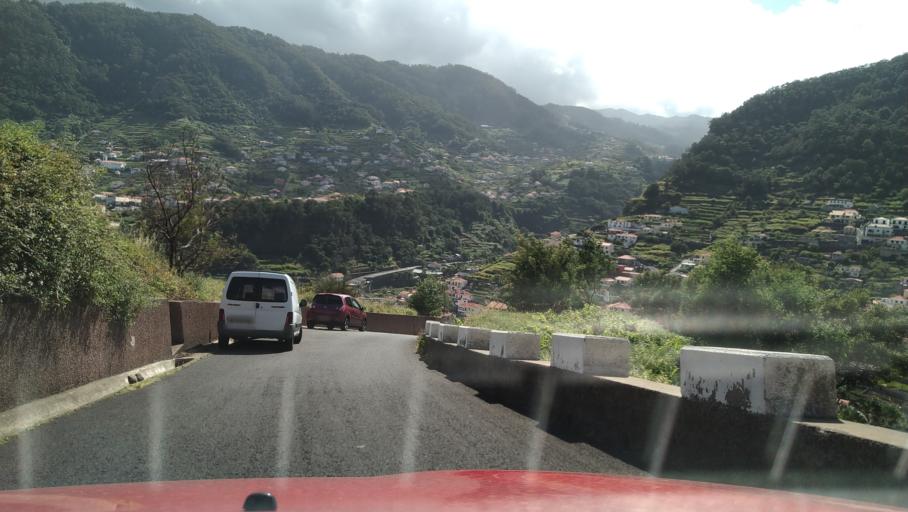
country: PT
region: Madeira
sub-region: Machico
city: Canical
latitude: 32.7361
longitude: -16.7748
